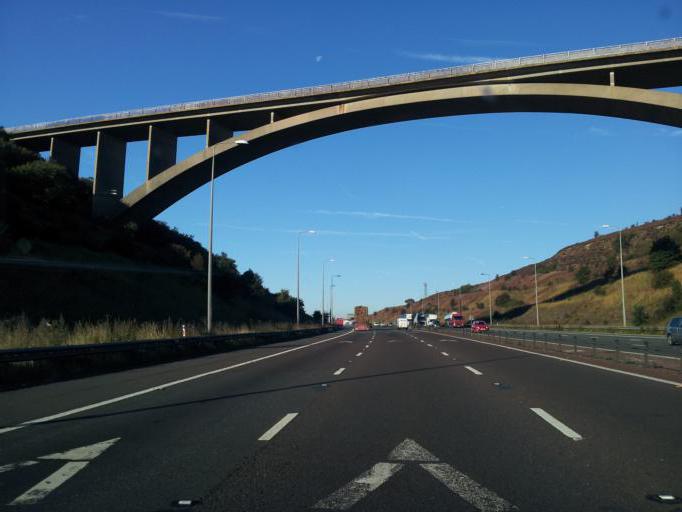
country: GB
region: England
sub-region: Calderdale
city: Ripponden
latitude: 53.6475
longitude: -1.9299
